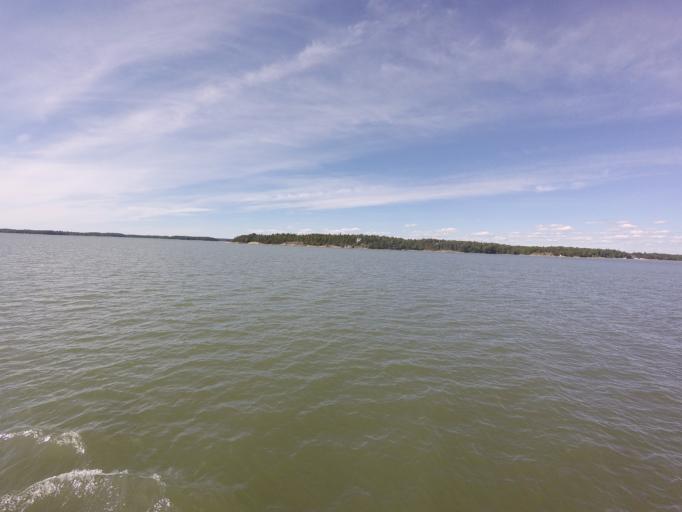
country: FI
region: Varsinais-Suomi
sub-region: Turku
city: Raisio
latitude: 60.4026
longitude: 22.1213
